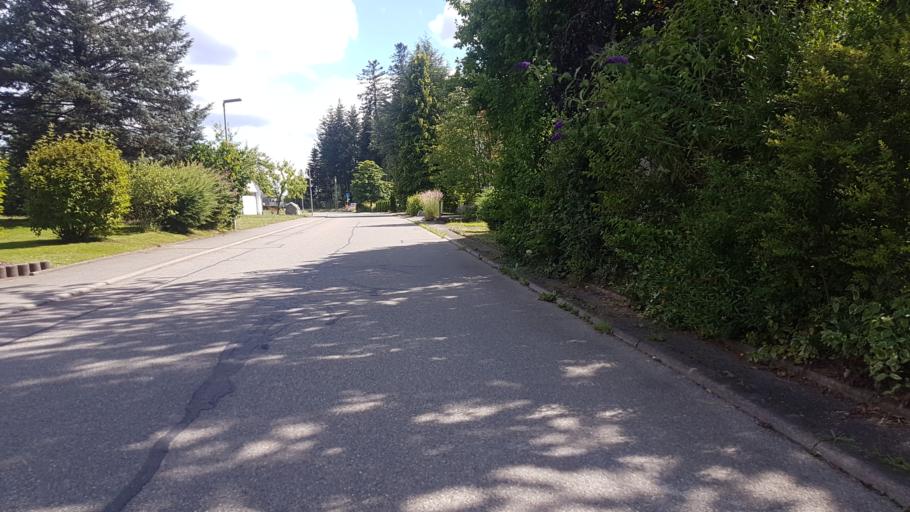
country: DE
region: Baden-Wuerttemberg
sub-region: Freiburg Region
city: Hardt
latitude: 48.1893
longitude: 8.4087
